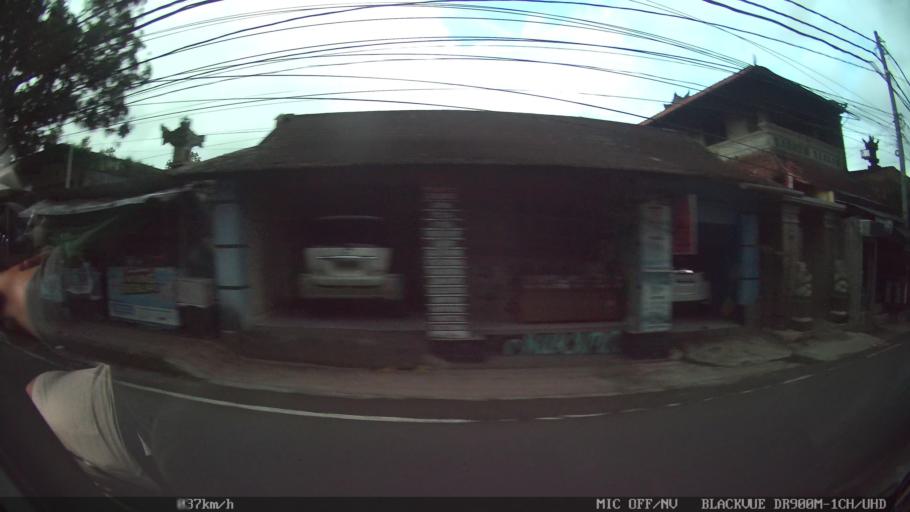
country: ID
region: Bali
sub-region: Kabupaten Gianyar
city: Ubud
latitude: -8.4887
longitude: 115.2539
